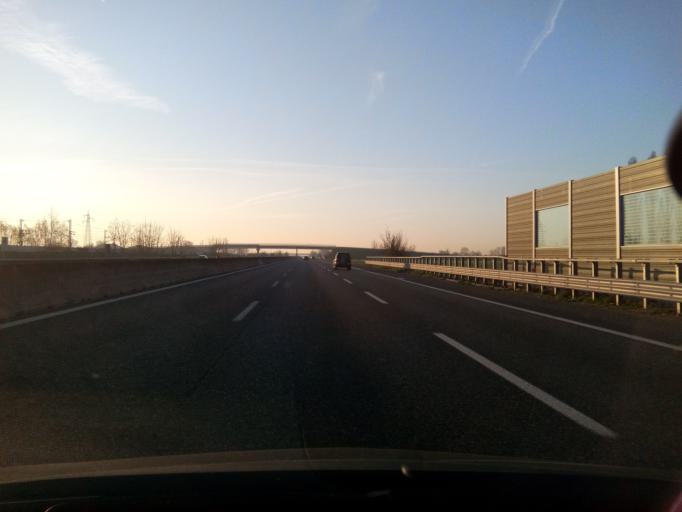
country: IT
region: Lombardy
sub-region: Provincia di Lodi
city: Pieve Fissiraga
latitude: 45.2666
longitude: 9.4623
